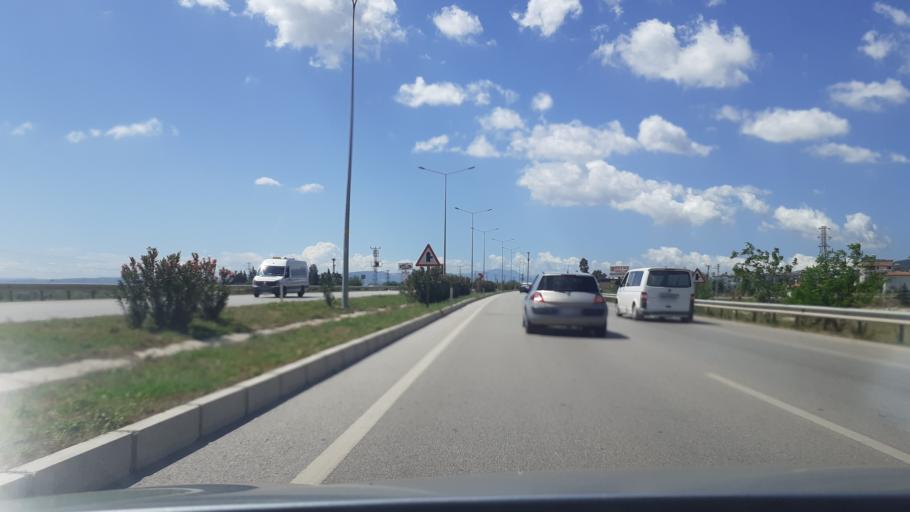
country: TR
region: Hatay
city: Serinyol
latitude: 36.3654
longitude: 36.2233
